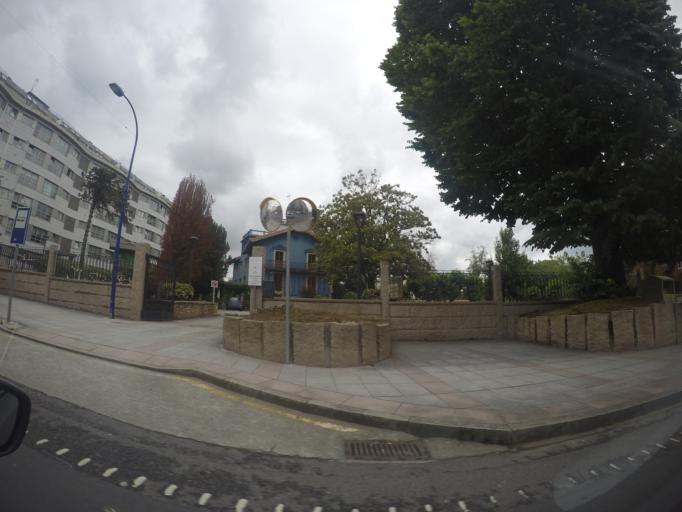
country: ES
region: Galicia
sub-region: Provincia da Coruna
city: Culleredo
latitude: 43.3114
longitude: -8.3826
